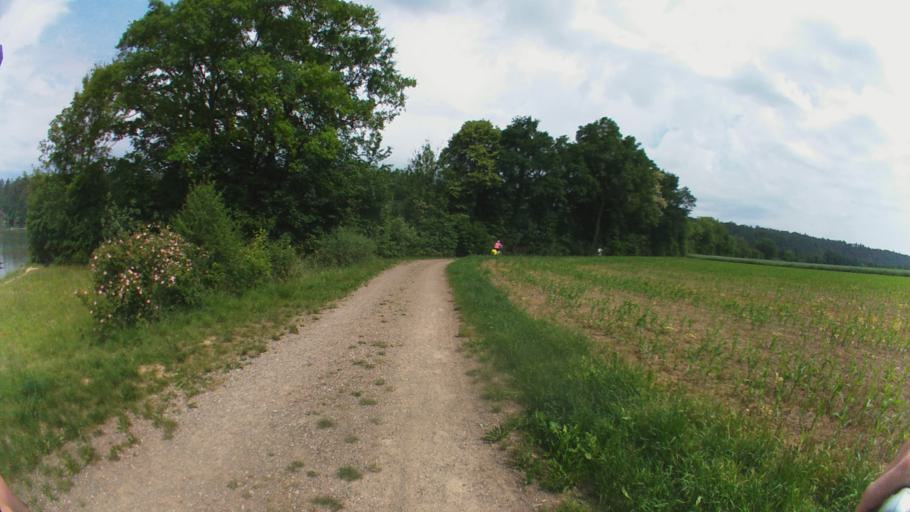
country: CH
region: Zurich
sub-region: Bezirk Buelach
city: Glattfelden
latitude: 47.5782
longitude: 8.4914
